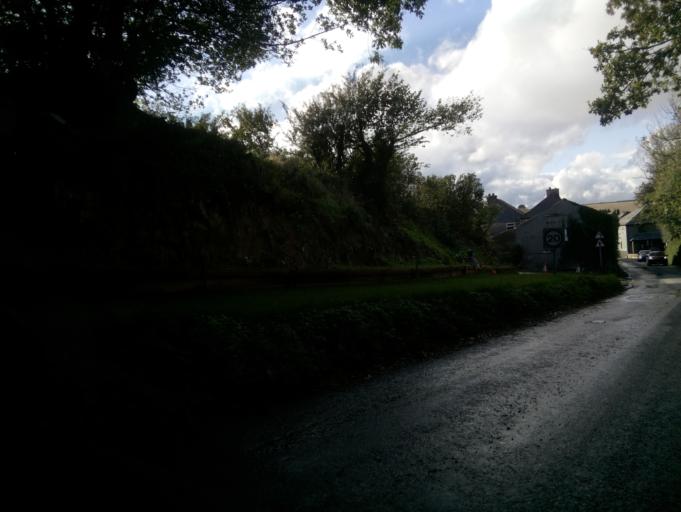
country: GB
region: England
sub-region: Devon
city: Totnes
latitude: 50.3613
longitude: -3.7332
